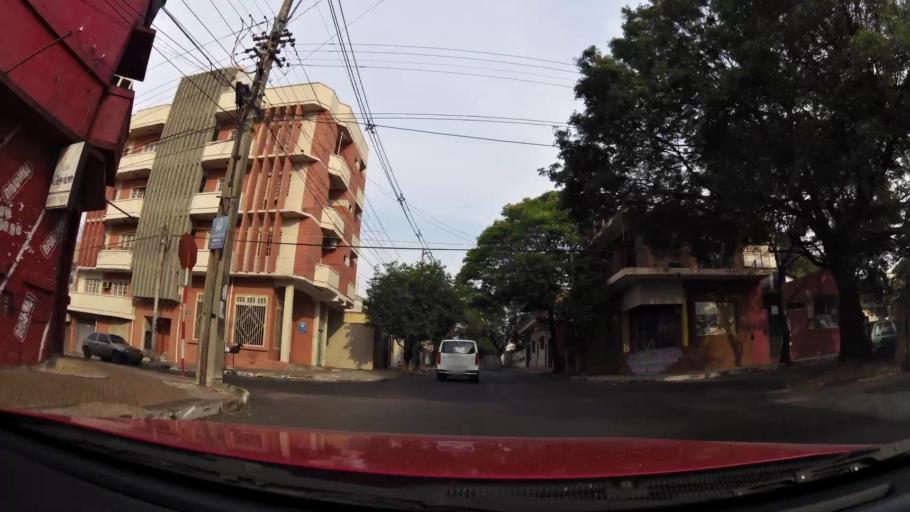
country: PY
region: Asuncion
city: Asuncion
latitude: -25.2981
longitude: -57.6292
